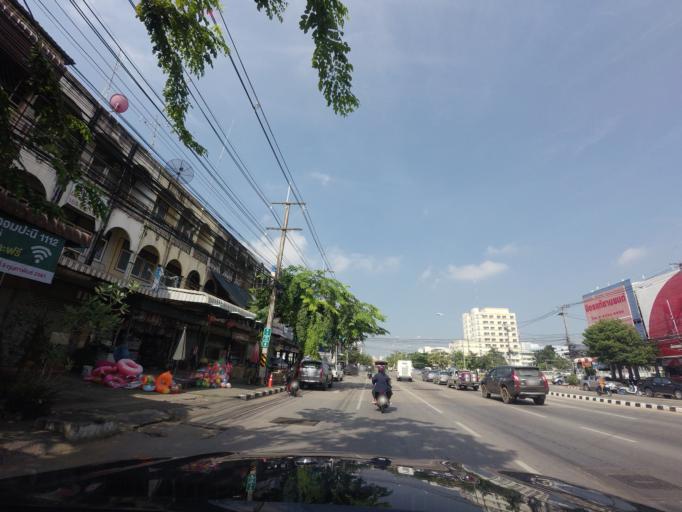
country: TH
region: Khon Kaen
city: Khon Kaen
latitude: 16.4286
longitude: 102.8520
